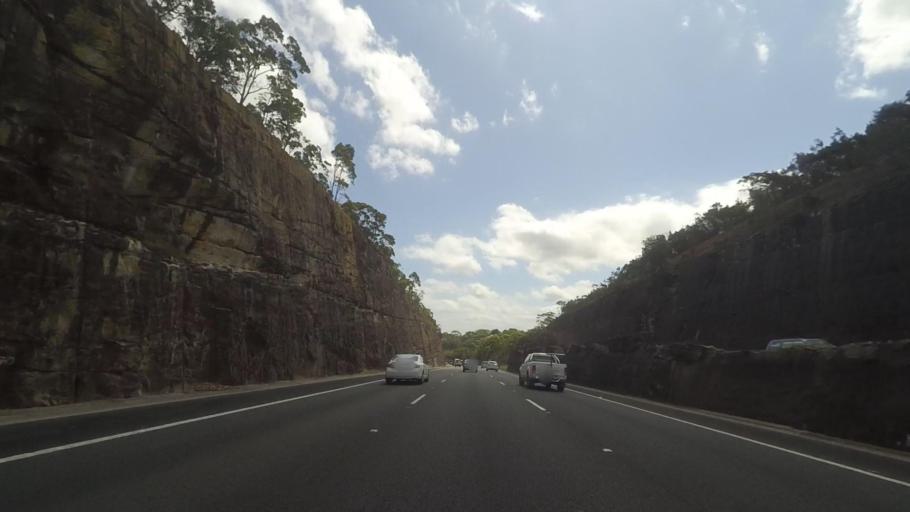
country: AU
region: New South Wales
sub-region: Hornsby Shire
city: Berowra
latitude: -33.5868
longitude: 151.1789
